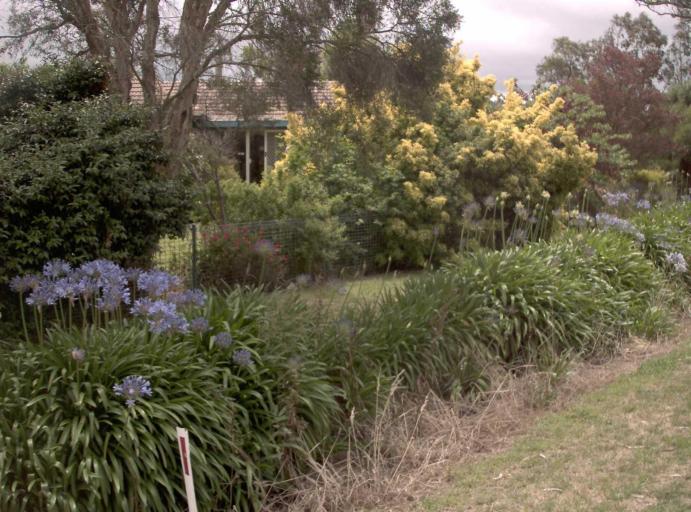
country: AU
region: Victoria
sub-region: Latrobe
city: Traralgon
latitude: -38.5147
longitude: 146.6485
